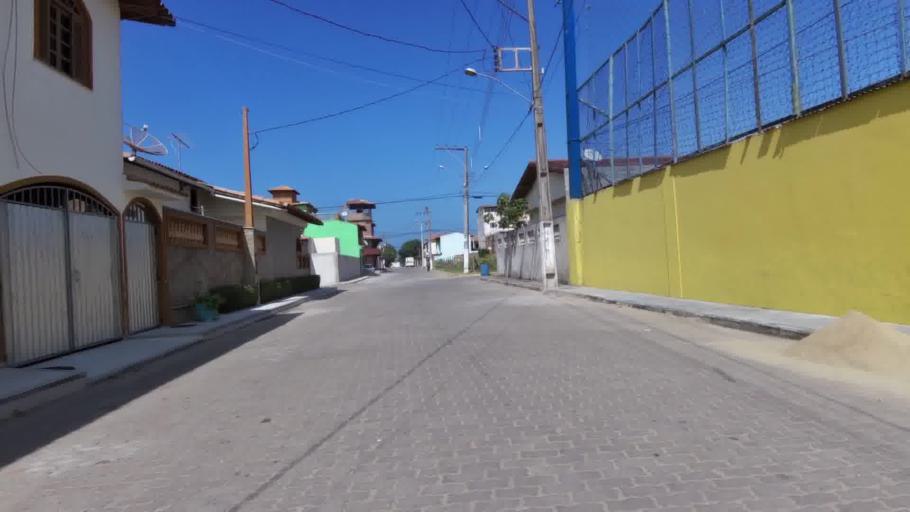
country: BR
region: Espirito Santo
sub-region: Marataizes
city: Marataizes
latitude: -21.0293
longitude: -40.8158
